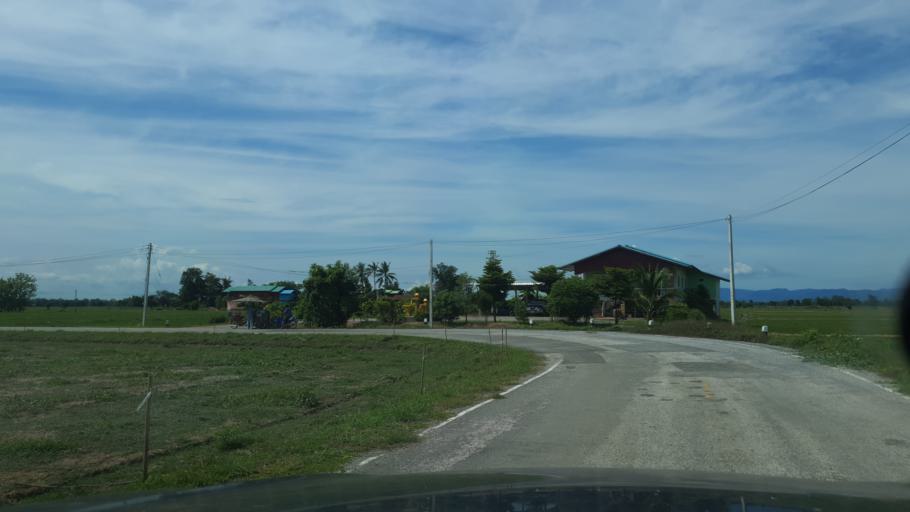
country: TH
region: Sukhothai
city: Si Samrong
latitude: 17.1979
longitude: 99.7246
